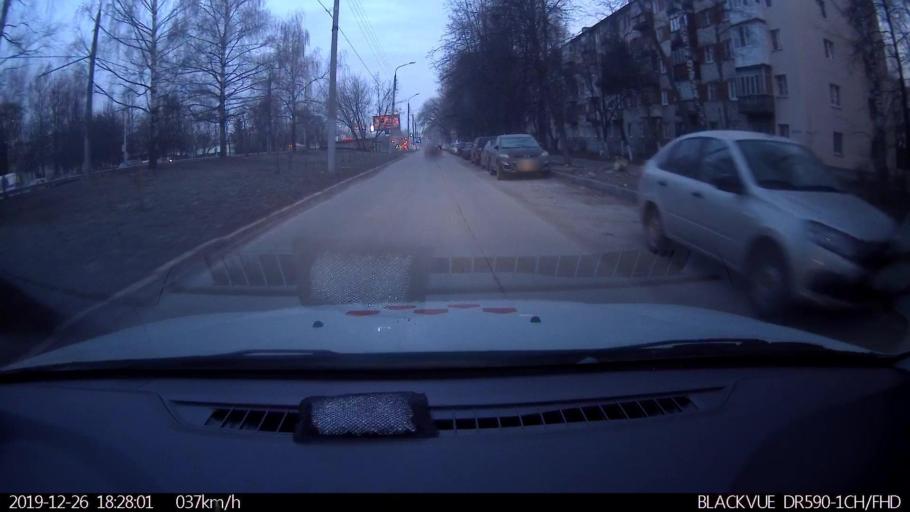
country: RU
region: Nizjnij Novgorod
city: Nizhniy Novgorod
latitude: 56.2932
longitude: 44.0356
